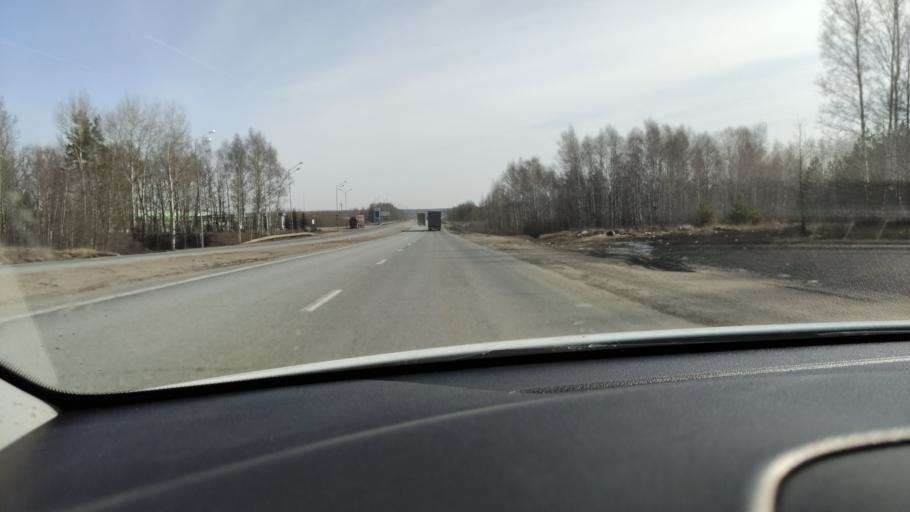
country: RU
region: Tatarstan
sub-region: Gorod Kazan'
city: Kazan
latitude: 55.9142
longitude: 49.1121
